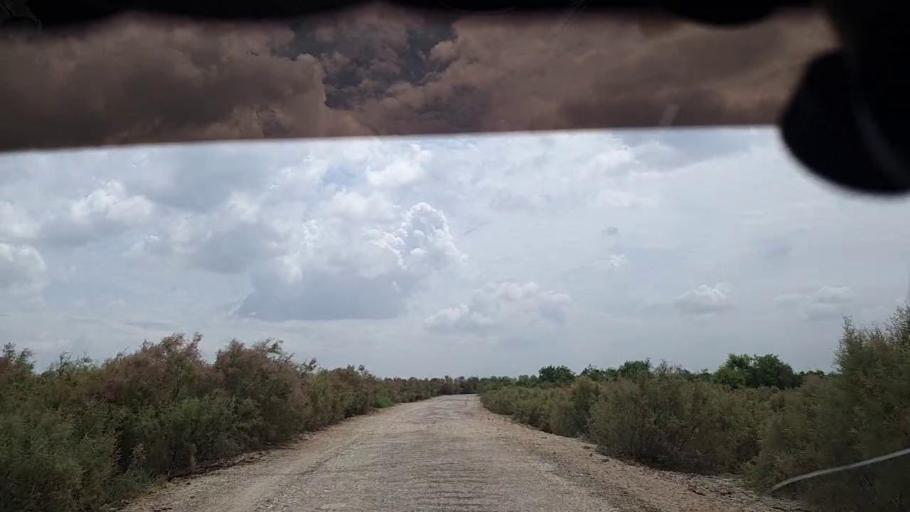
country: PK
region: Sindh
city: Ghauspur
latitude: 28.0637
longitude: 68.9399
